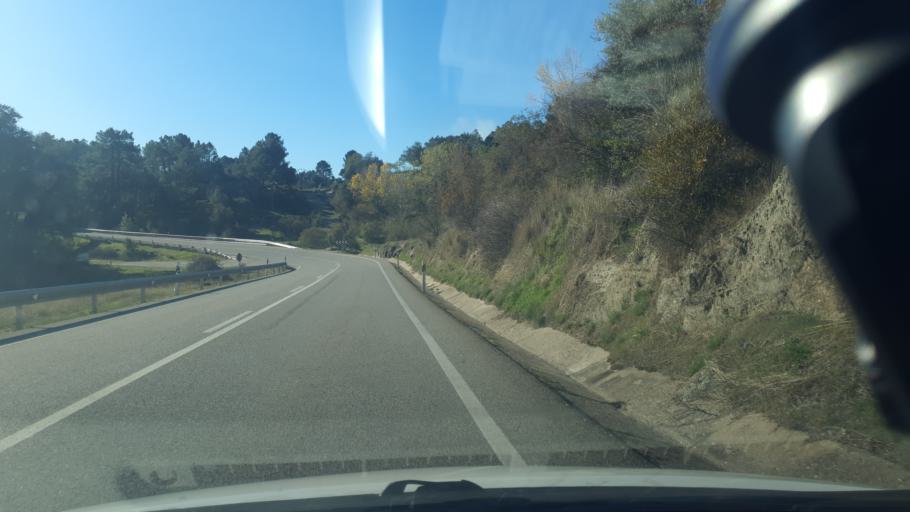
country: ES
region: Castille and Leon
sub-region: Provincia de Avila
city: Mombeltran
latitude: 40.2223
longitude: -5.0359
